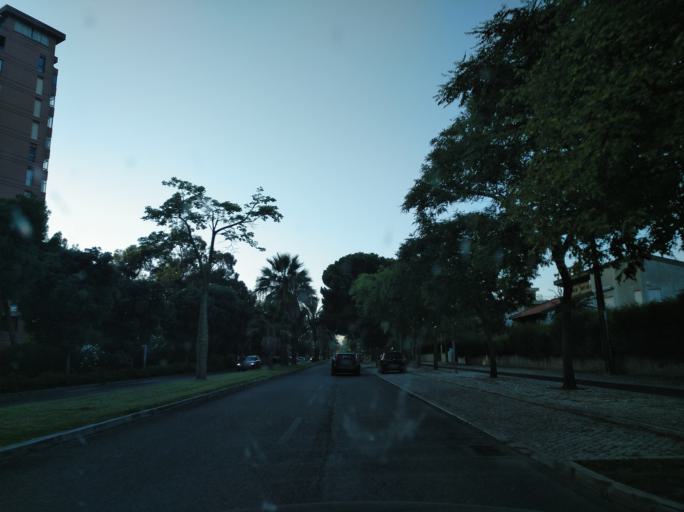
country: PT
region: Setubal
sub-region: Almada
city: Trafaria
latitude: 38.6594
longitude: -9.2411
